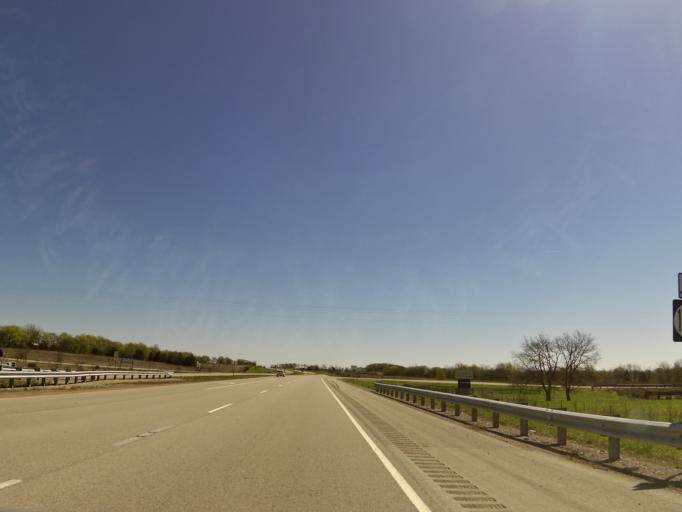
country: US
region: Kentucky
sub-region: Logan County
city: Auburn
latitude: 36.8915
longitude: -86.6438
